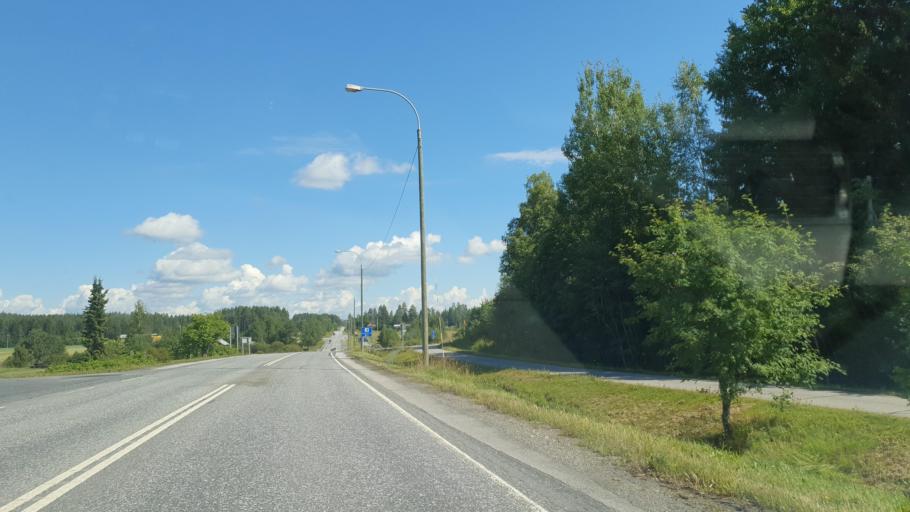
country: FI
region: Northern Savo
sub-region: Ylae-Savo
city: Iisalmi
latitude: 63.6374
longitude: 27.2296
